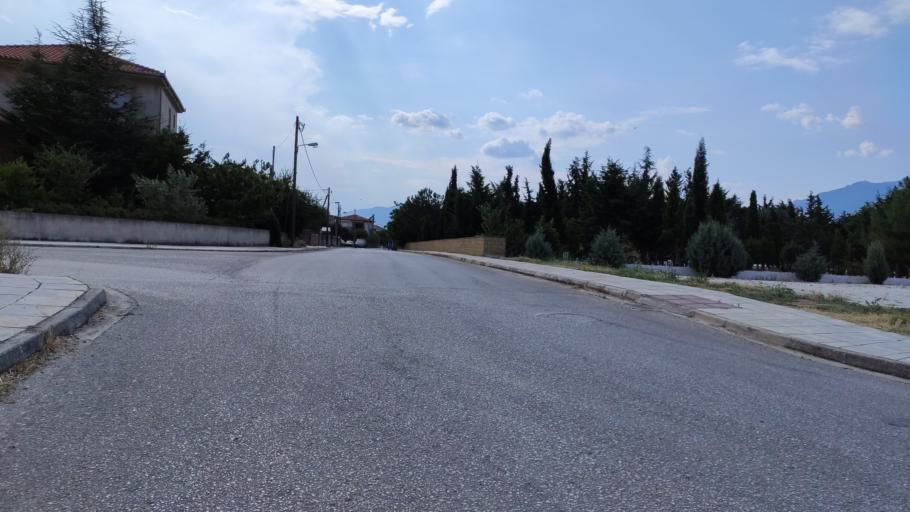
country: GR
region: East Macedonia and Thrace
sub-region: Nomos Rodopis
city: Komotini
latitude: 41.1313
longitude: 25.4020
